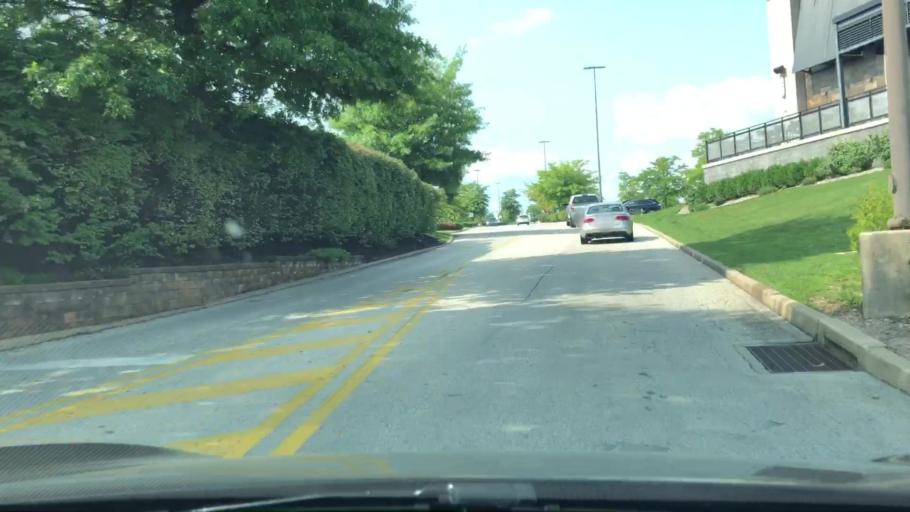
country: US
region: Pennsylvania
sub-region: Montgomery County
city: King of Prussia
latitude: 40.0875
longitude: -75.3956
